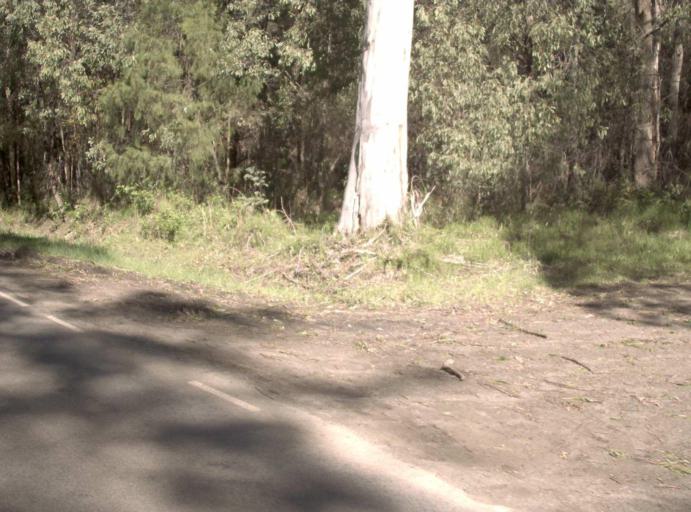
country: AU
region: Victoria
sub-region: Yarra Ranges
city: Millgrove
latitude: -37.8771
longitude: 145.8424
